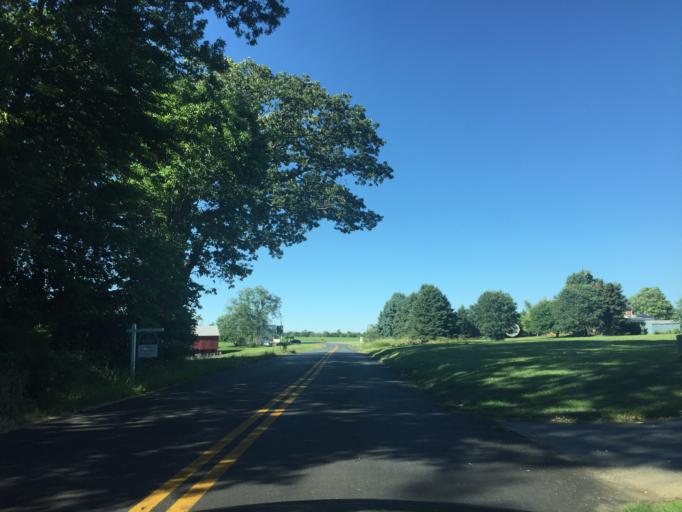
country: US
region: Maryland
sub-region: Carroll County
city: Westminster
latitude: 39.5724
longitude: -76.9195
